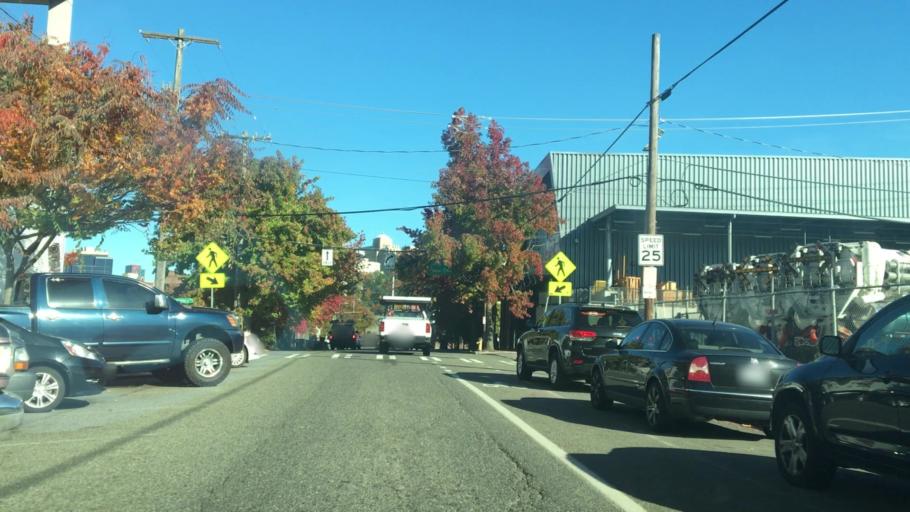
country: US
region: Washington
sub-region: King County
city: Seattle
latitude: 47.5946
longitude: -122.3238
